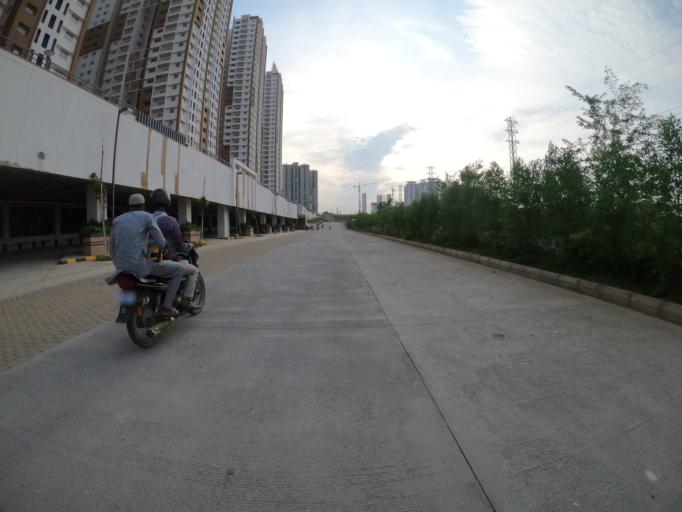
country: IN
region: Telangana
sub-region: Hyderabad
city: Hyderabad
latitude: 17.3998
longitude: 78.3552
